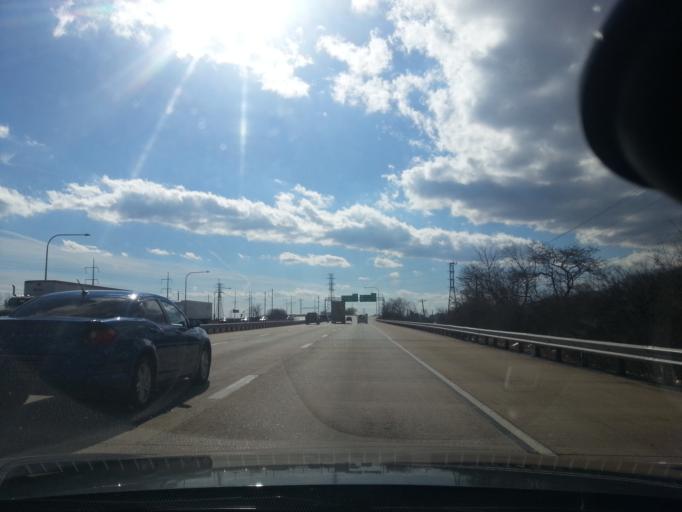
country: US
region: Delaware
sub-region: New Castle County
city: Edgemoor
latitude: 39.7559
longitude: -75.4950
